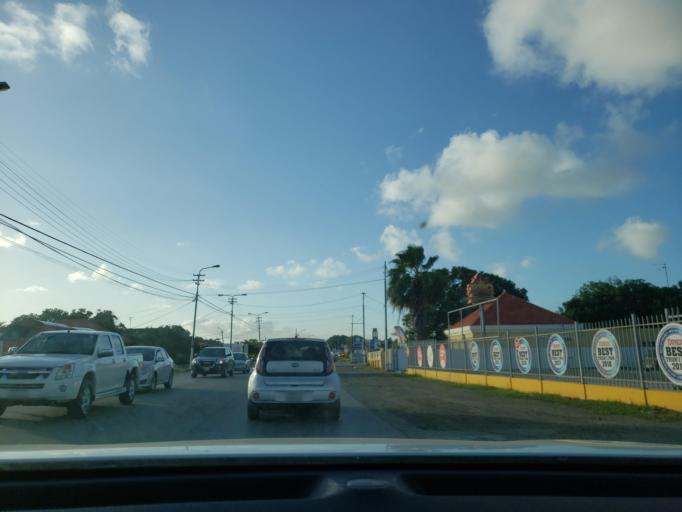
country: CW
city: Willemstad
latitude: 12.1041
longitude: -68.8879
